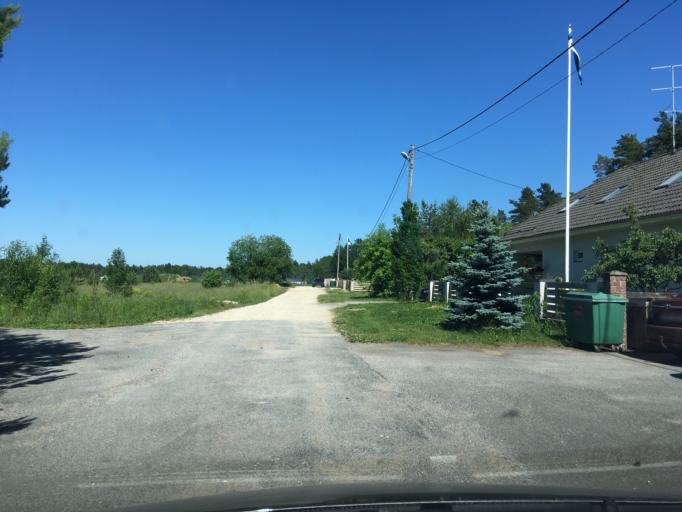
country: EE
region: Harju
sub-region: Raasiku vald
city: Raasiku
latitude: 59.1779
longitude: 25.1729
